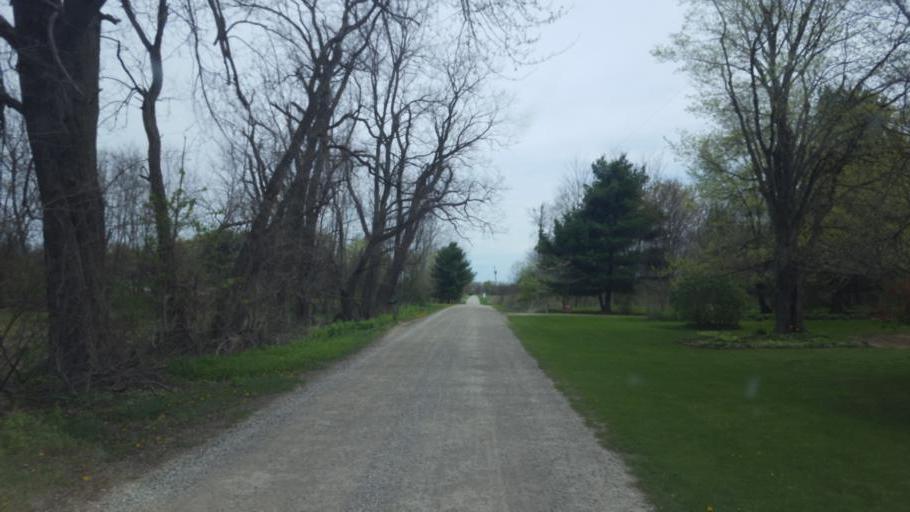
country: US
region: Ohio
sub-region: Knox County
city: Fredericktown
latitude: 40.5117
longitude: -82.6593
